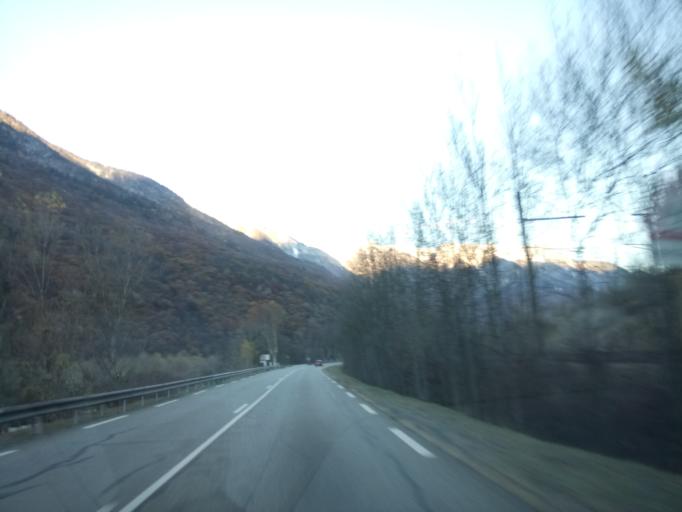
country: FR
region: Rhone-Alpes
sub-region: Departement de la Savoie
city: La Chambre
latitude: 45.3581
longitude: 6.2918
